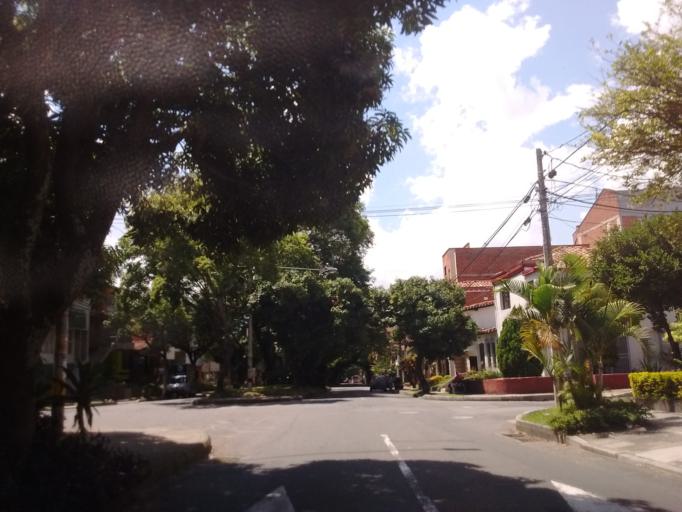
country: CO
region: Antioquia
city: Medellin
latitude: 6.2438
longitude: -75.6056
